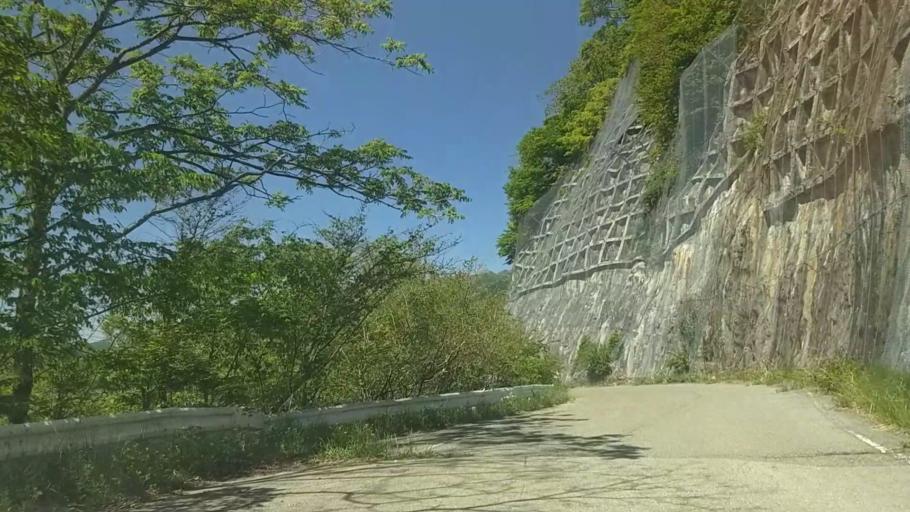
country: JP
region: Yamanashi
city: Nirasaki
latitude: 35.8786
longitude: 138.4531
